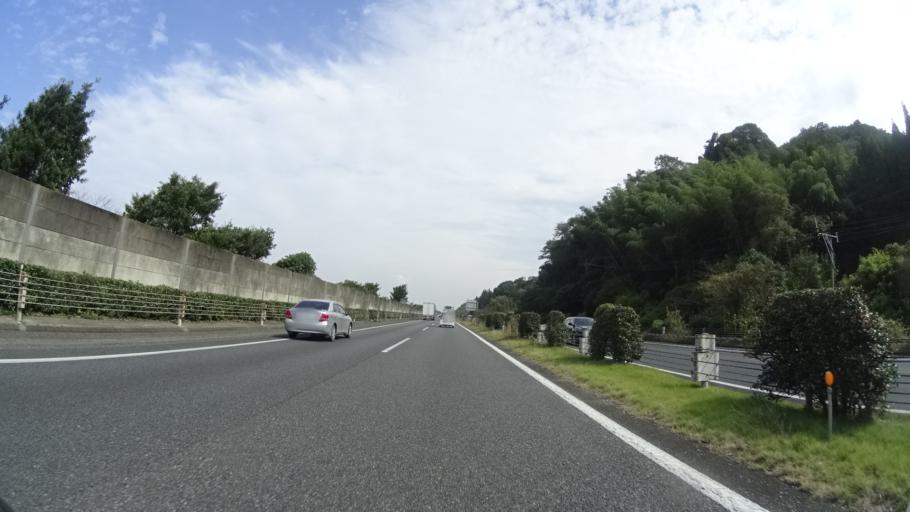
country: JP
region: Kumamoto
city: Yatsushiro
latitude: 32.5242
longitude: 130.6610
